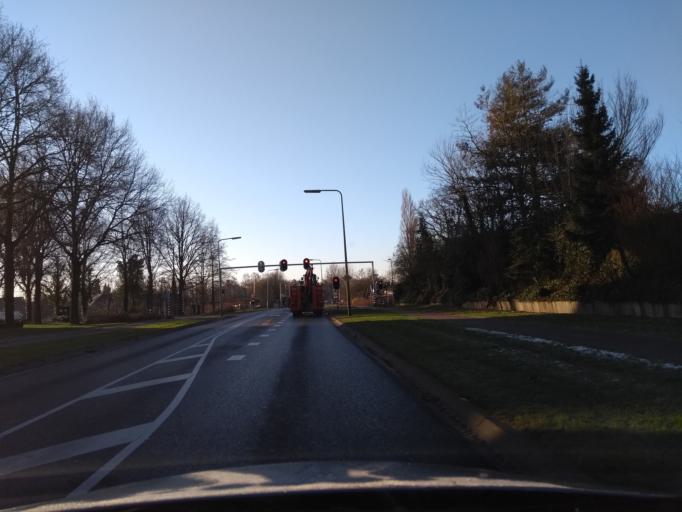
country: NL
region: Overijssel
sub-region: Gemeente Hof van Twente
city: Delden
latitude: 52.2591
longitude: 6.7017
